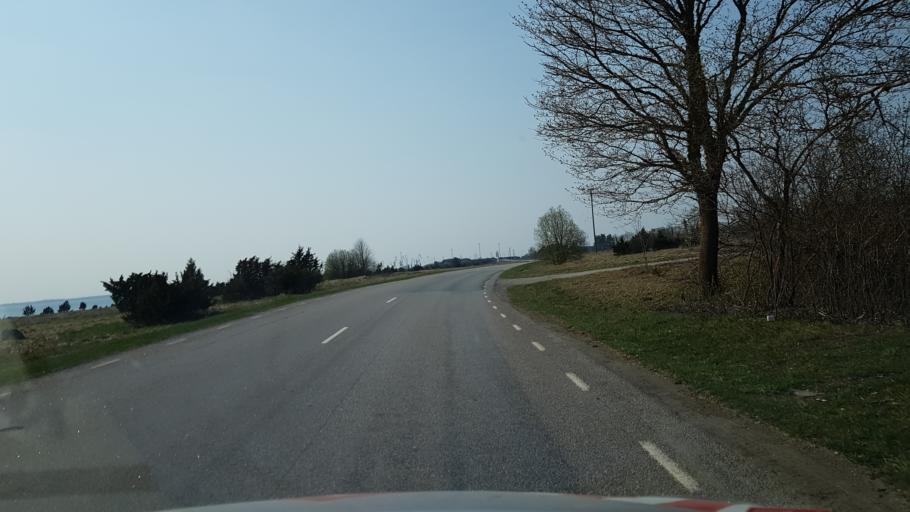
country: EE
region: Harju
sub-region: Paldiski linn
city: Paldiski
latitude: 59.3289
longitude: 24.1097
